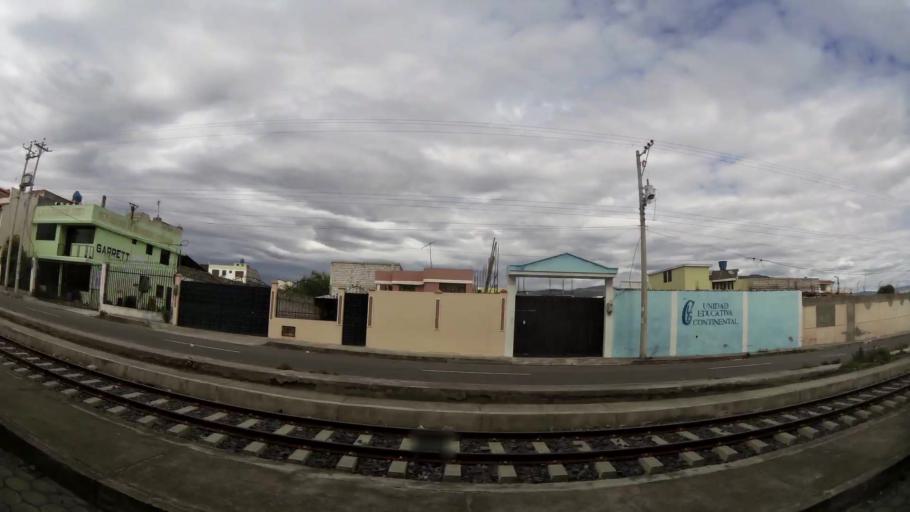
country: EC
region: Cotopaxi
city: Latacunga
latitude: -0.9419
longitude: -78.6180
